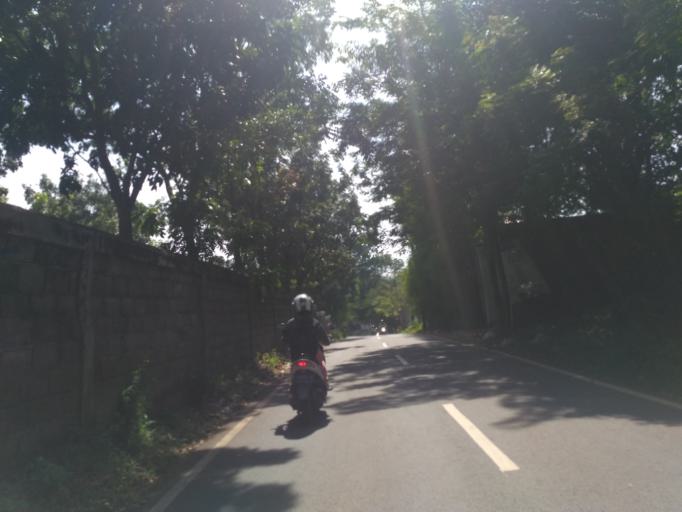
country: ID
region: Central Java
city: Semarang
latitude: -7.0265
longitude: 110.4107
